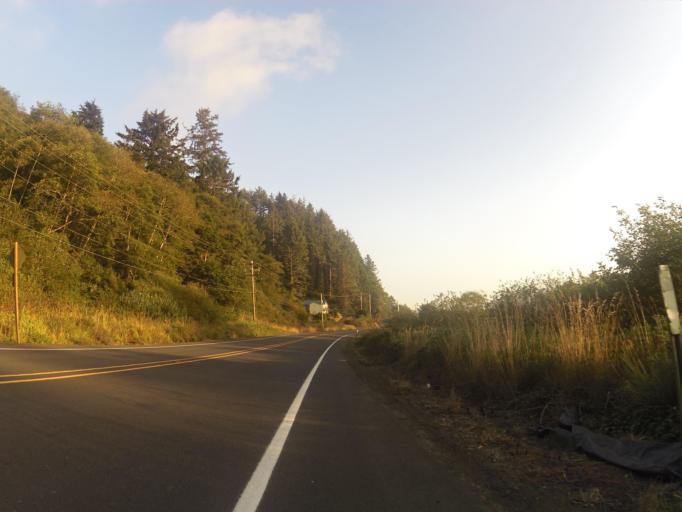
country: US
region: Oregon
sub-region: Tillamook County
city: Rockaway Beach
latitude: 45.5721
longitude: -123.9435
